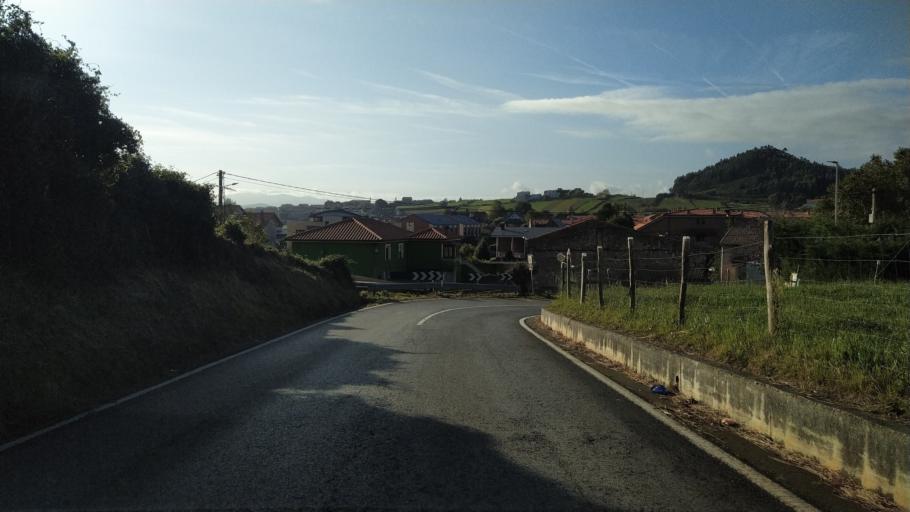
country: ES
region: Cantabria
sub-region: Provincia de Cantabria
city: Santa Cruz de Bezana
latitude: 43.4478
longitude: -3.9244
